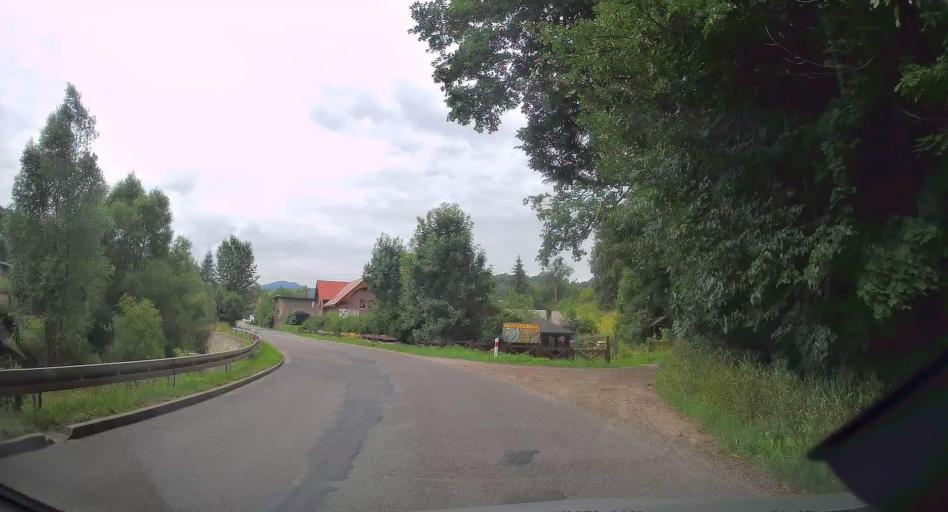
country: PL
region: Lower Silesian Voivodeship
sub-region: Powiat walbrzyski
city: Jedlina-Zdroj
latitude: 50.7277
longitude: 16.3836
